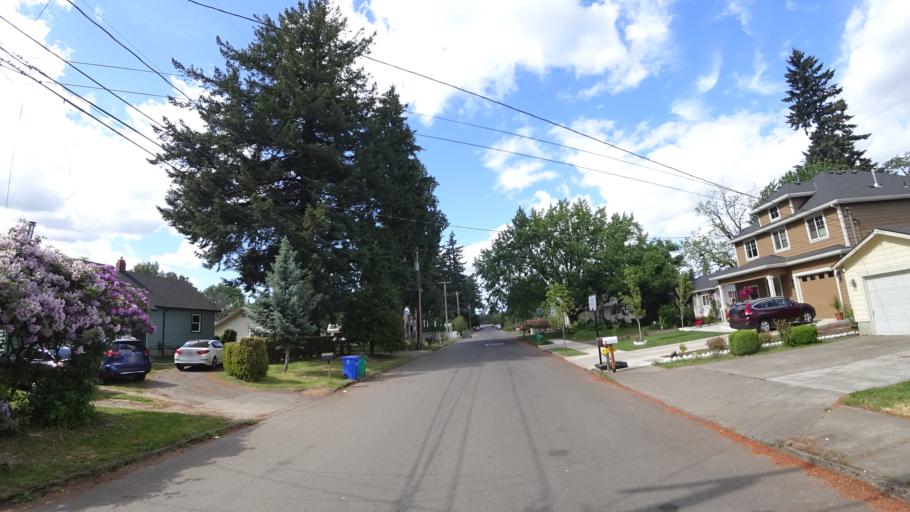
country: US
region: Oregon
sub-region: Multnomah County
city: Lents
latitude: 45.5016
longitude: -122.5493
